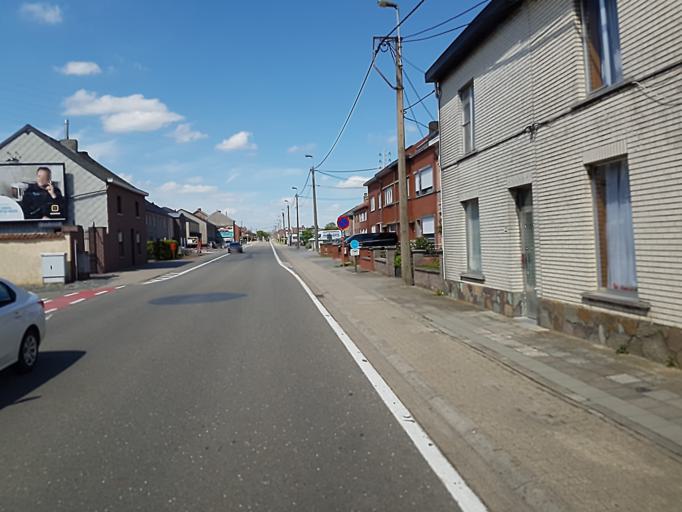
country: BE
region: Flanders
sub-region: Provincie Vlaams-Brabant
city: Tienen
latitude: 50.8175
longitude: 4.9264
